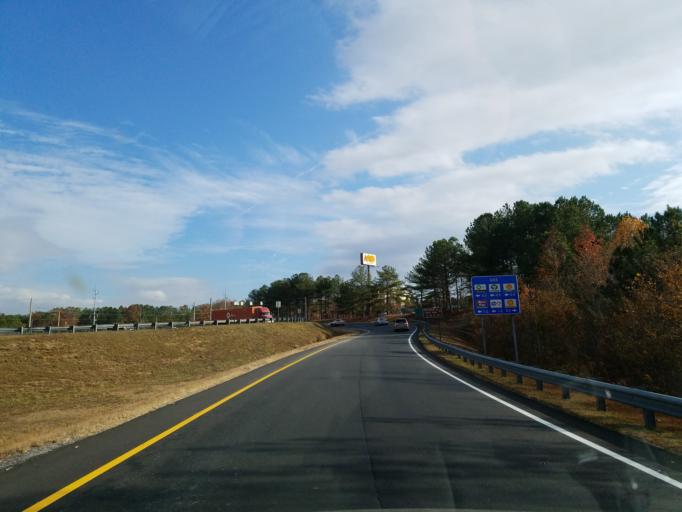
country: US
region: Georgia
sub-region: Cobb County
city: Austell
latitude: 33.7761
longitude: -84.6072
